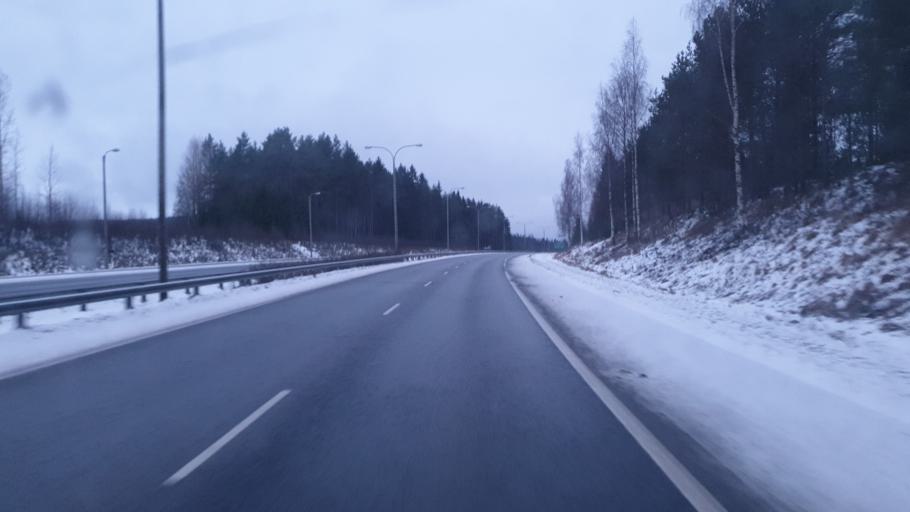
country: FI
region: Northern Savo
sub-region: Kuopio
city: Siilinjaervi
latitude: 63.0554
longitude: 27.6710
